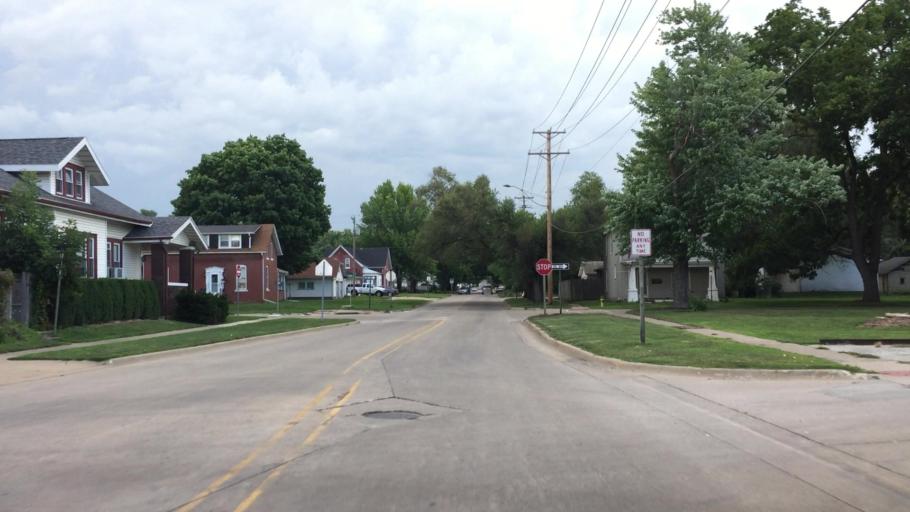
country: US
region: Iowa
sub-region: Lee County
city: Fort Madison
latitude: 40.6306
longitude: -91.3246
